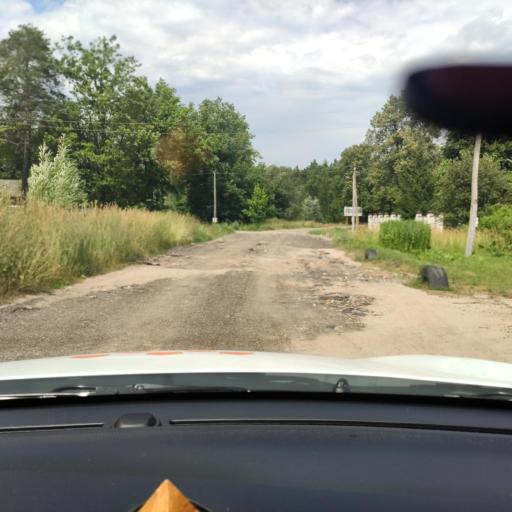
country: RU
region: Tatarstan
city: Osinovo
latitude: 55.9095
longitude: 48.9619
